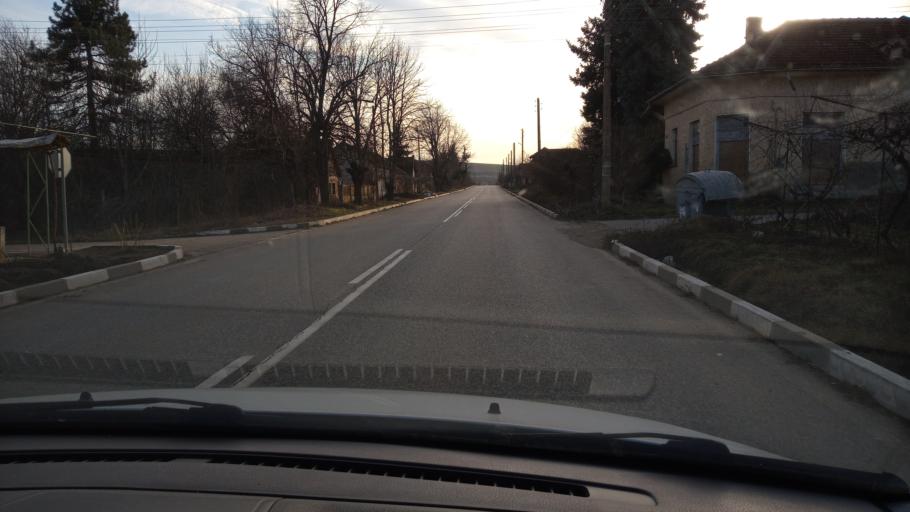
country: BG
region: Pleven
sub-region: Obshtina Pleven
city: Slavyanovo
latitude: 43.5520
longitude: 24.8642
